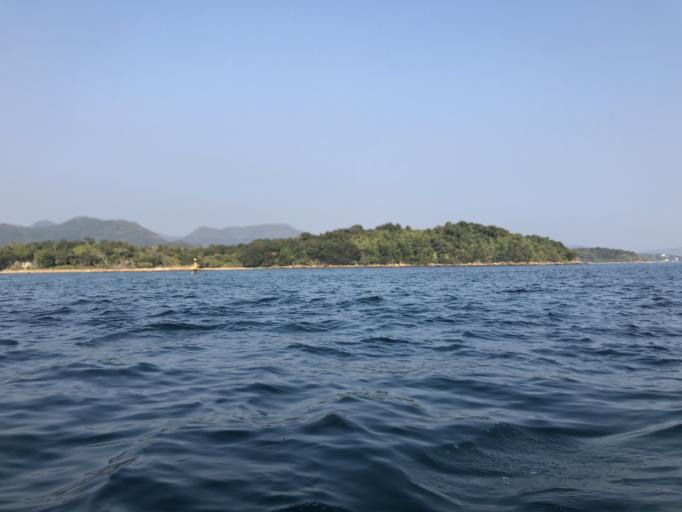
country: HK
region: Sai Kung
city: Sai Kung
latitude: 22.3784
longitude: 114.2779
